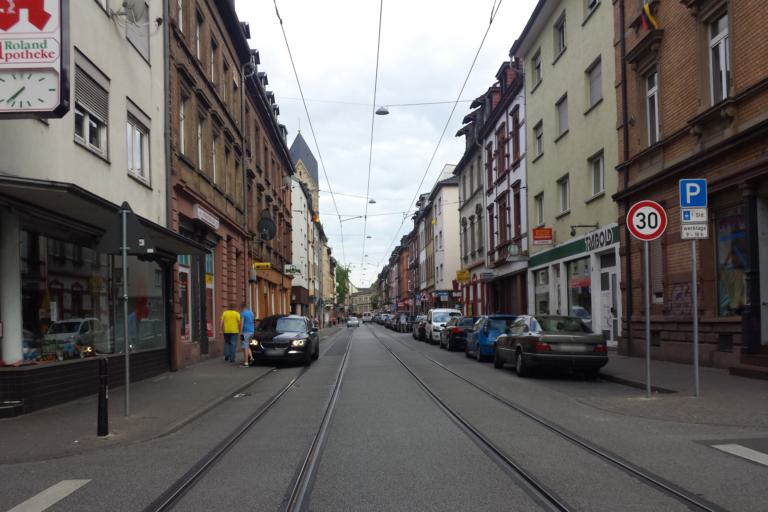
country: DE
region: Baden-Wuerttemberg
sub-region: Karlsruhe Region
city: Mannheim
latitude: 49.5010
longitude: 8.4642
